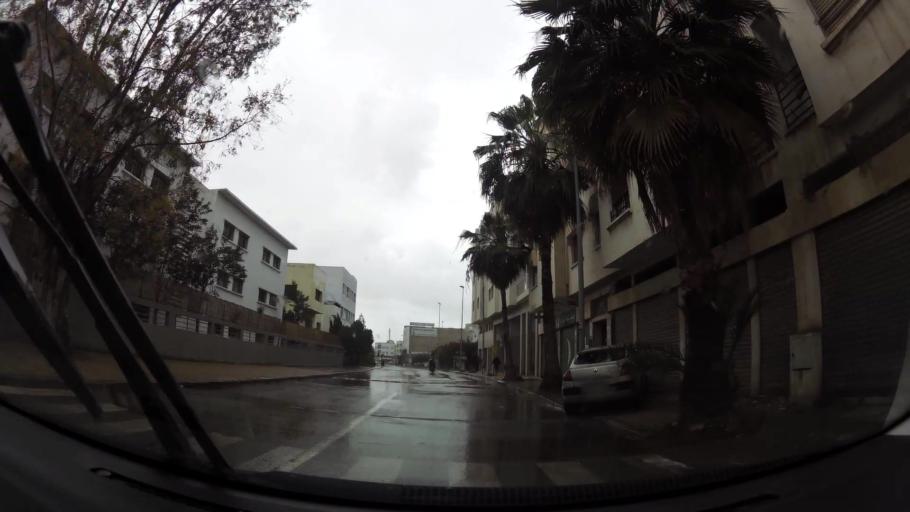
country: MA
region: Grand Casablanca
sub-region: Casablanca
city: Casablanca
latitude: 33.5434
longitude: -7.6719
